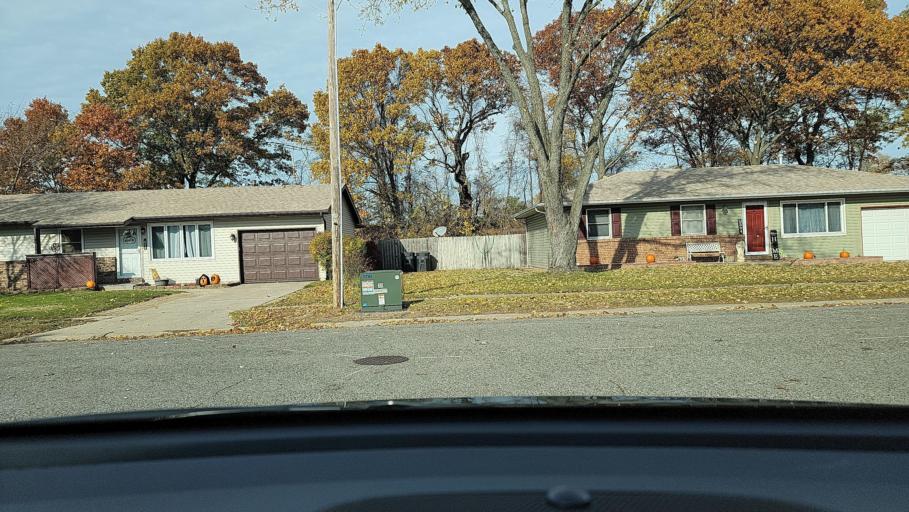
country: US
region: Indiana
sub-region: Lake County
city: Lake Station
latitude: 41.5818
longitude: -87.2097
